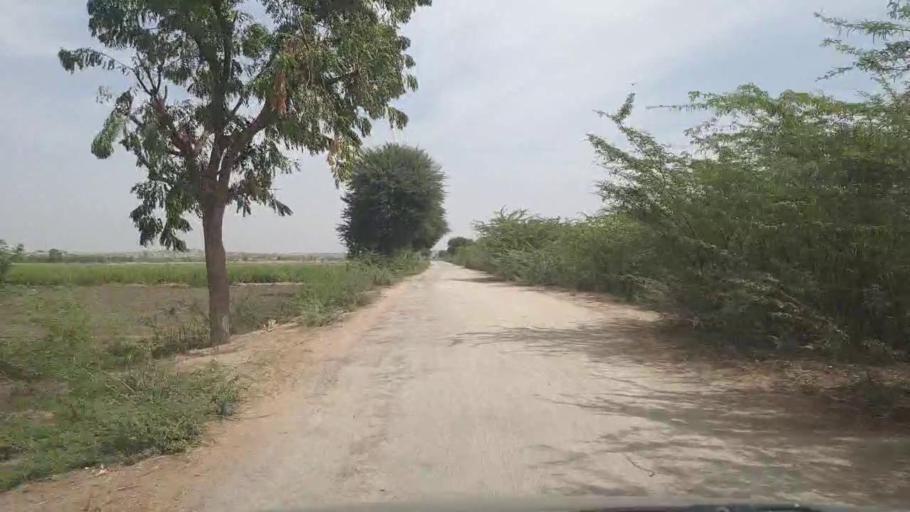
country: PK
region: Sindh
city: Umarkot
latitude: 25.2253
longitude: 69.7018
